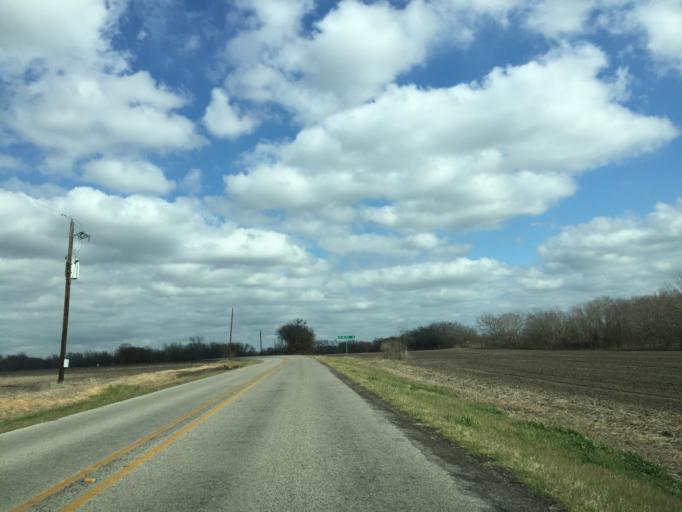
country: US
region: Texas
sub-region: Williamson County
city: Granger
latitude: 30.7082
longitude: -97.4633
